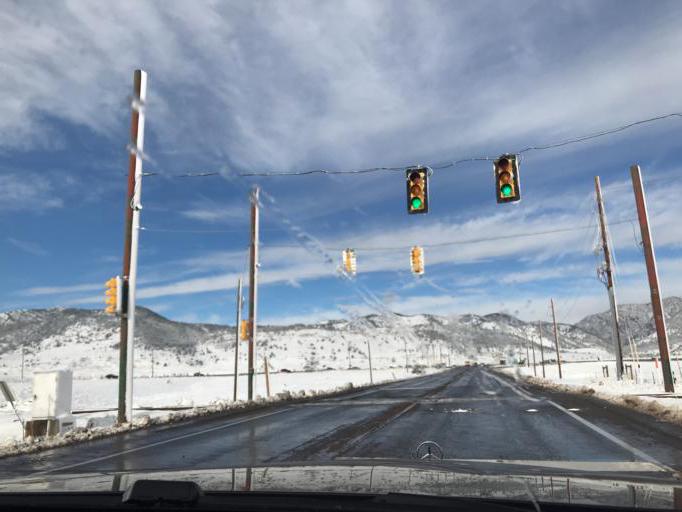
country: US
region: Colorado
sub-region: Boulder County
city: Superior
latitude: 39.8656
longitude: -105.2363
